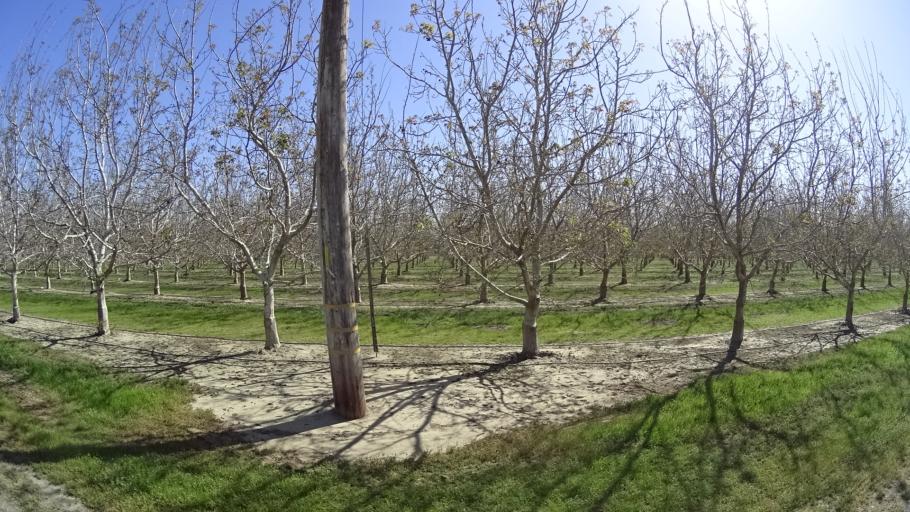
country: US
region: California
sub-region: Glenn County
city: Hamilton City
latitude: 39.7182
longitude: -122.0103
